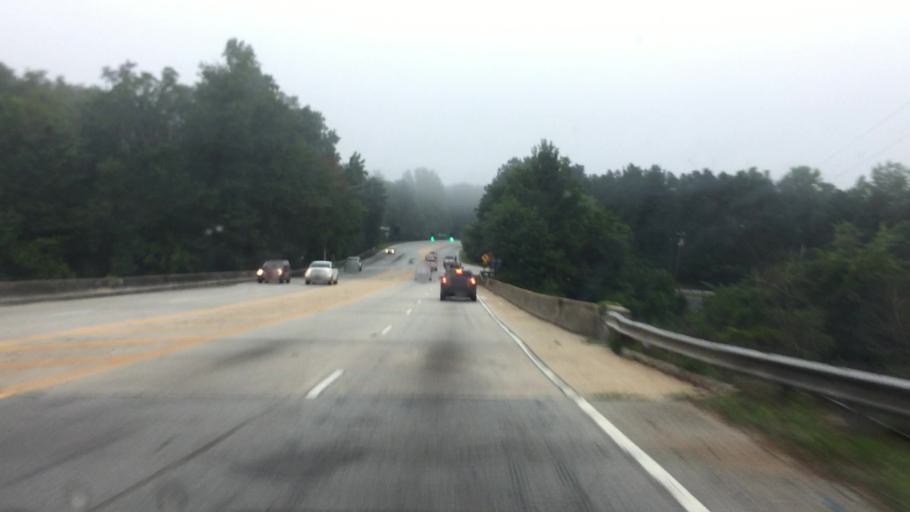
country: US
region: Georgia
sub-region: DeKalb County
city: Pine Mountain
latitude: 33.6529
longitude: -84.1873
